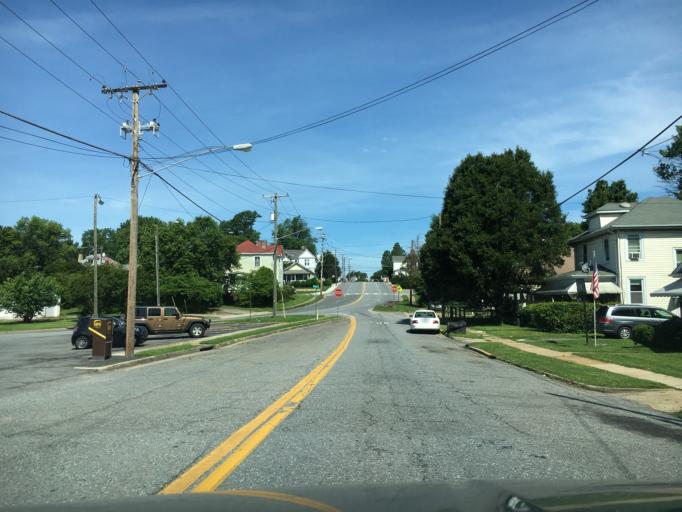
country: US
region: Virginia
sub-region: City of Lynchburg
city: West Lynchburg
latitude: 37.3964
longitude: -79.1669
